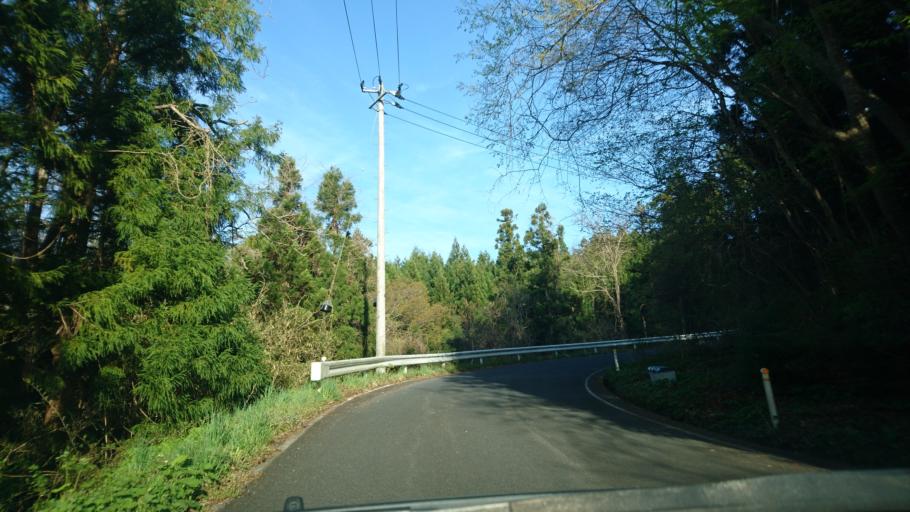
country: JP
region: Iwate
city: Ichinoseki
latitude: 38.8901
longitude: 141.2917
